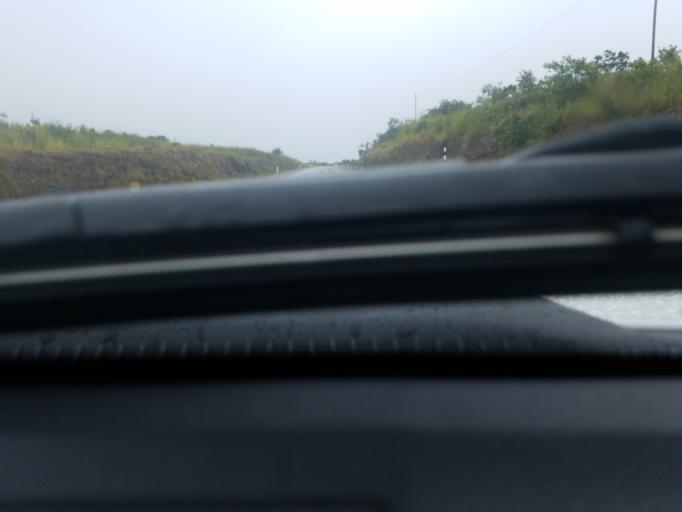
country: TZ
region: Kigoma
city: Mwandiga
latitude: -4.6585
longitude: 29.7227
